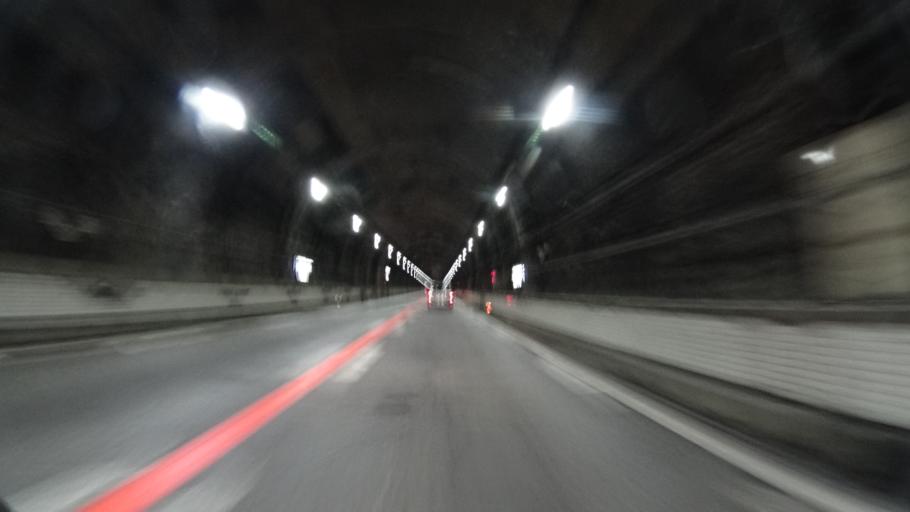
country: JP
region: Nagano
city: Iida
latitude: 35.4593
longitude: 137.6687
